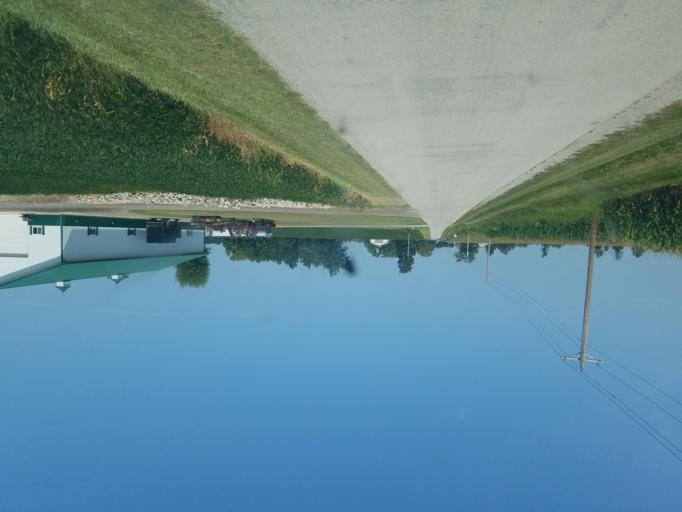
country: US
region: Ohio
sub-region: Crawford County
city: Bucyrus
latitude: 40.8671
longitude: -83.1124
